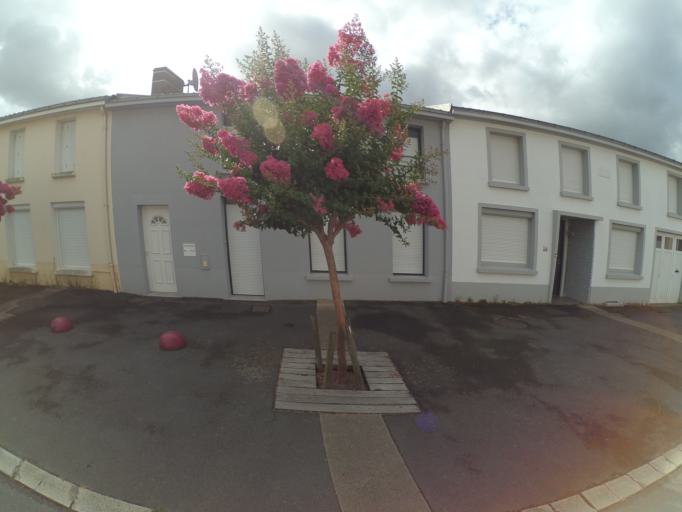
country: FR
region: Pays de la Loire
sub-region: Departement de Maine-et-Loire
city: Villedieu-la-Blouere
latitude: 47.1474
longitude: -1.0632
